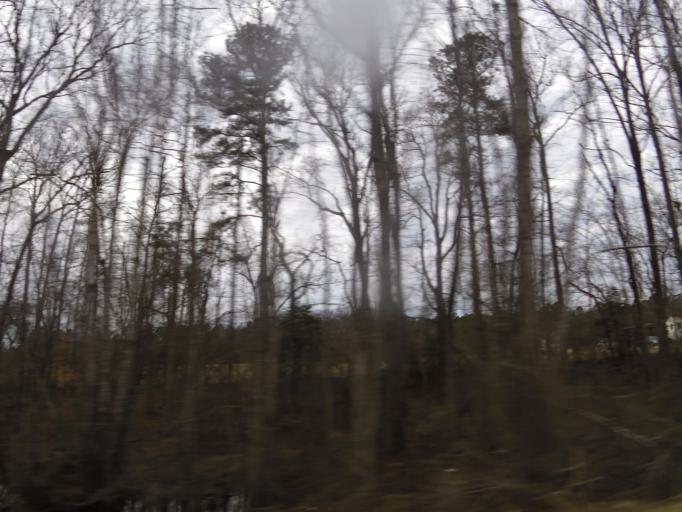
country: US
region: North Carolina
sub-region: Hertford County
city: Murfreesboro
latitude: 36.3685
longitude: -77.1669
